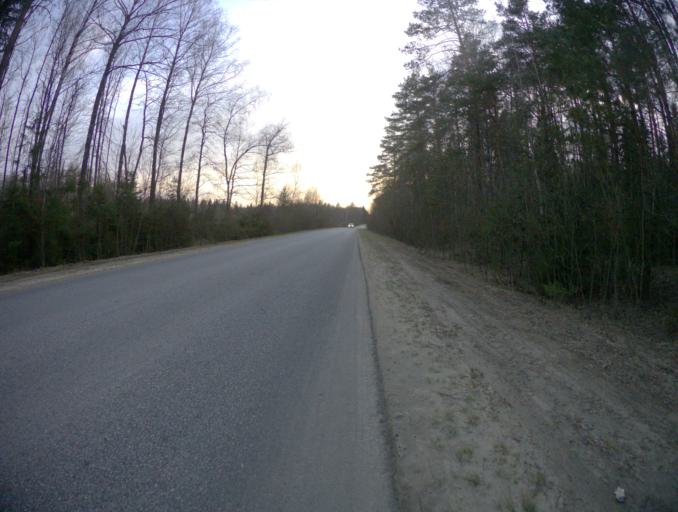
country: RU
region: Vladimir
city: Kommunar
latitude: 56.0698
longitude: 40.5136
